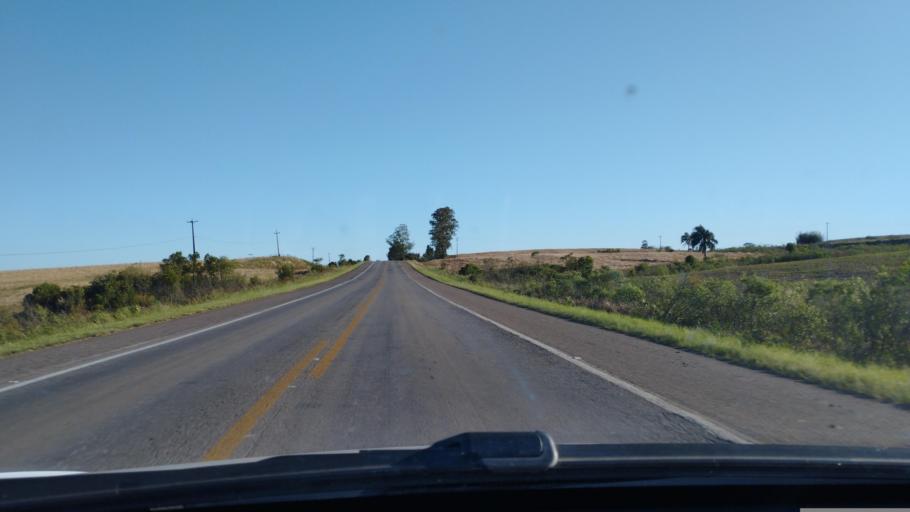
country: BR
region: Rio Grande do Sul
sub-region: Julio De Castilhos
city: Julio de Castilhos
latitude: -29.3958
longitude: -53.6690
